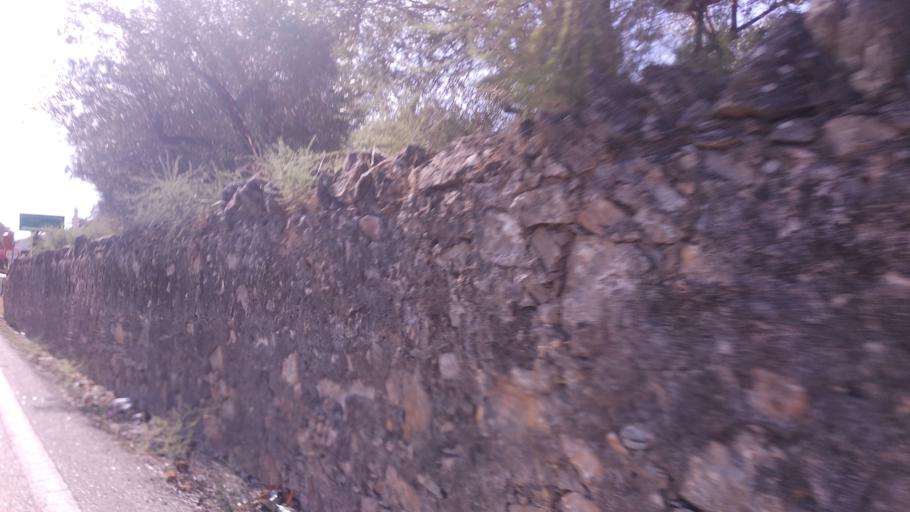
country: PT
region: Faro
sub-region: Sao Bras de Alportel
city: Sao Bras de Alportel
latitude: 37.1599
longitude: -7.8995
